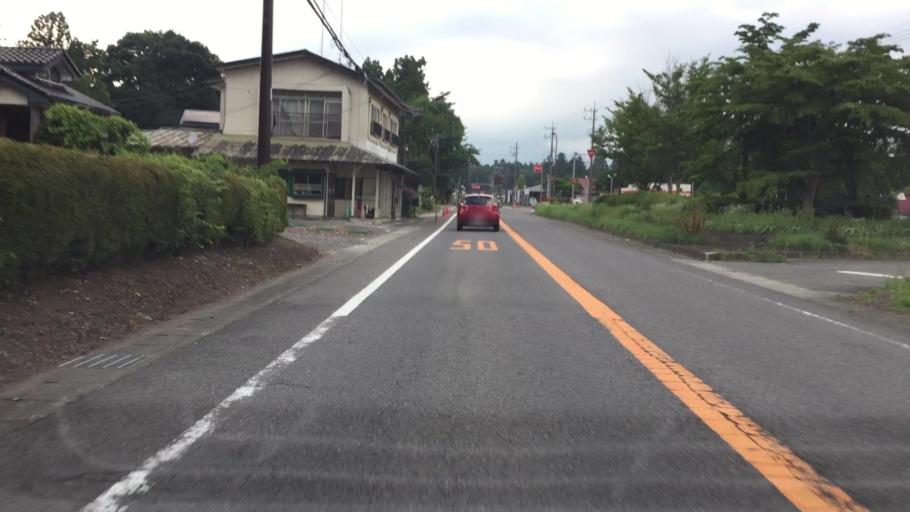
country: JP
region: Tochigi
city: Kuroiso
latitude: 37.0052
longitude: 140.0339
